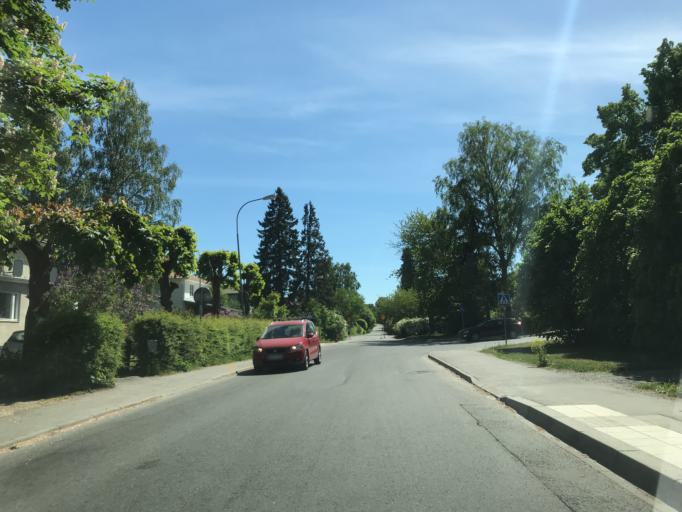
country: SE
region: Stockholm
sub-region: Sollentuna Kommun
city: Sollentuna
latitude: 59.4257
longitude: 17.9564
